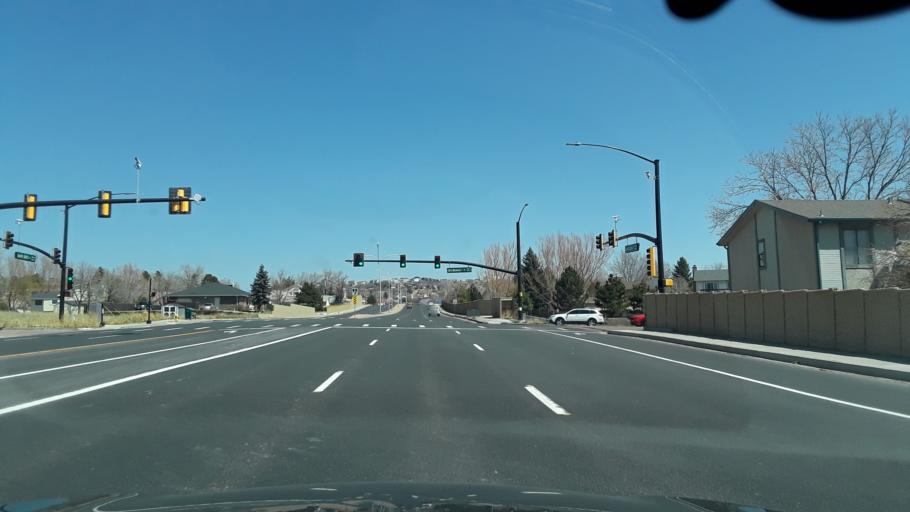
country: US
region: Colorado
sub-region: El Paso County
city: Cimarron Hills
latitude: 38.9013
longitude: -104.7425
